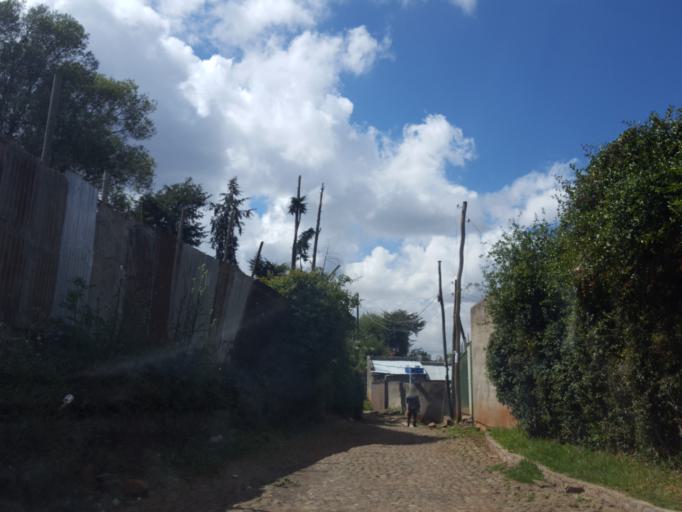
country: ET
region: Adis Abeba
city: Addis Ababa
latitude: 9.0703
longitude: 38.7360
